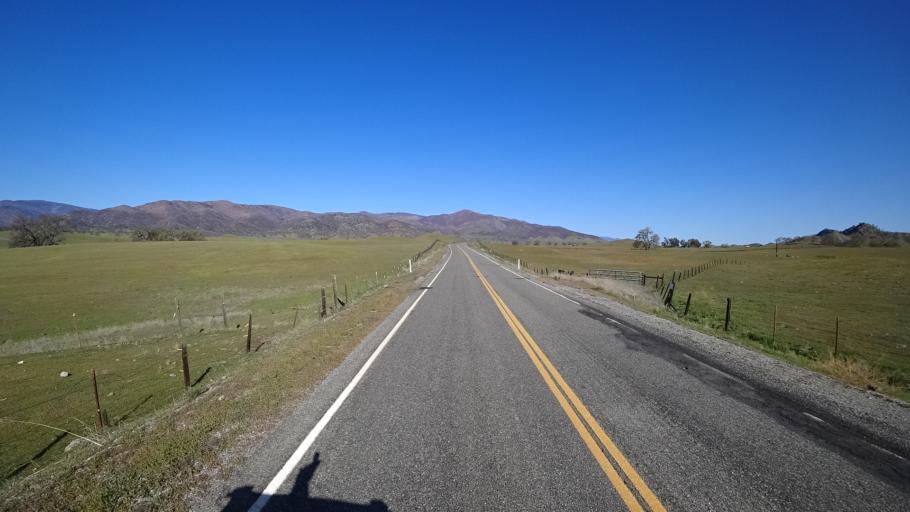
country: US
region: California
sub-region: Glenn County
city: Orland
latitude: 39.6870
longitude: -122.5417
